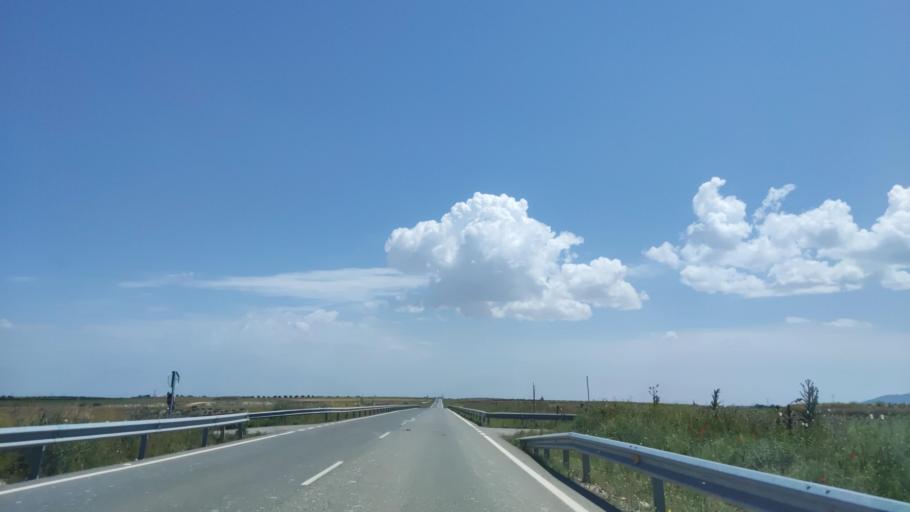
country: ES
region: Castille-La Mancha
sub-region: Province of Toledo
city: Mascaraque
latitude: 39.7135
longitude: -3.8322
